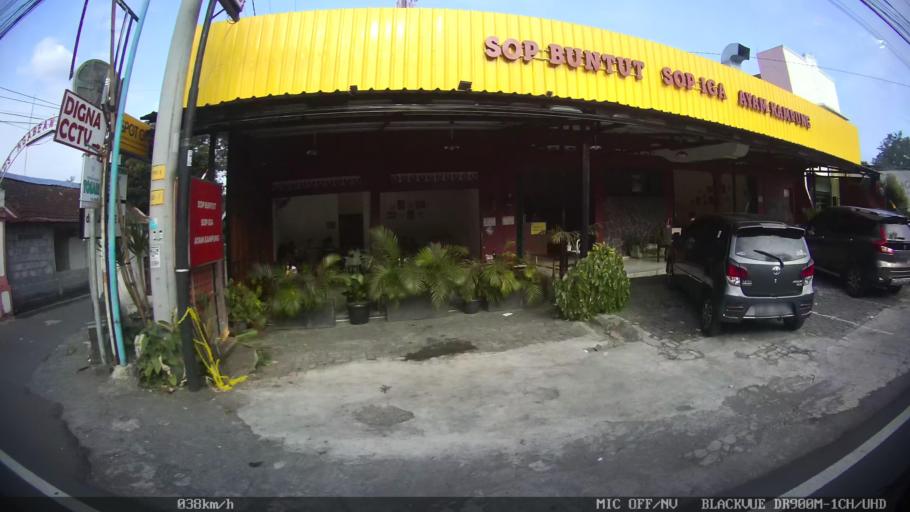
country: ID
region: Daerah Istimewa Yogyakarta
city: Melati
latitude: -7.7409
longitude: 110.3916
